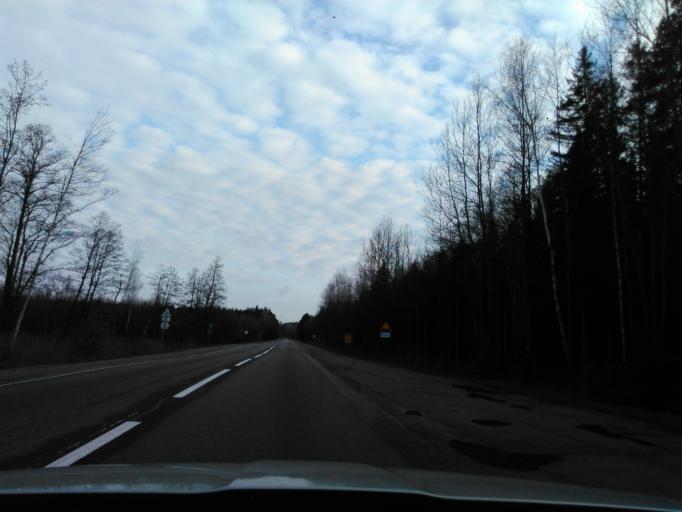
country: BY
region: Minsk
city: Plyeshchanitsy
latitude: 54.3916
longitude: 27.8711
